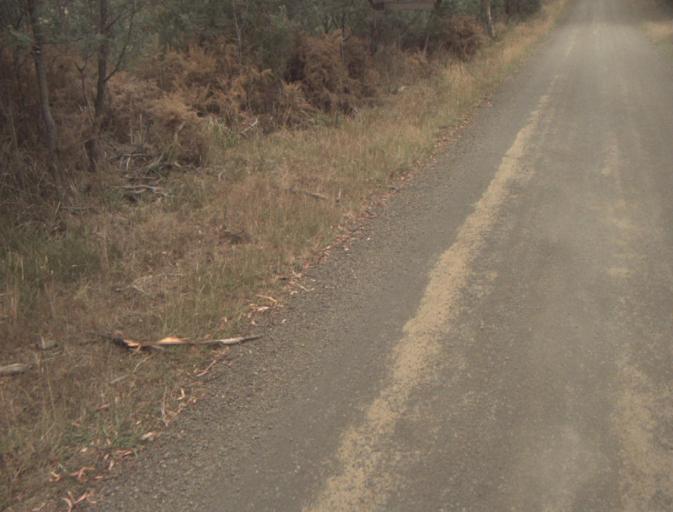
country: AU
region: Tasmania
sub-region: Northern Midlands
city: Evandale
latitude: -41.5283
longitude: 147.3581
